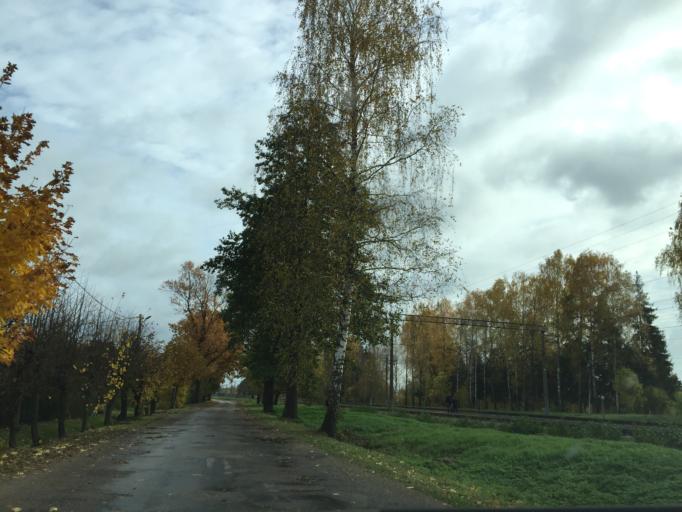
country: LV
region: Lielvarde
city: Lielvarde
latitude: 56.7215
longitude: 24.8156
